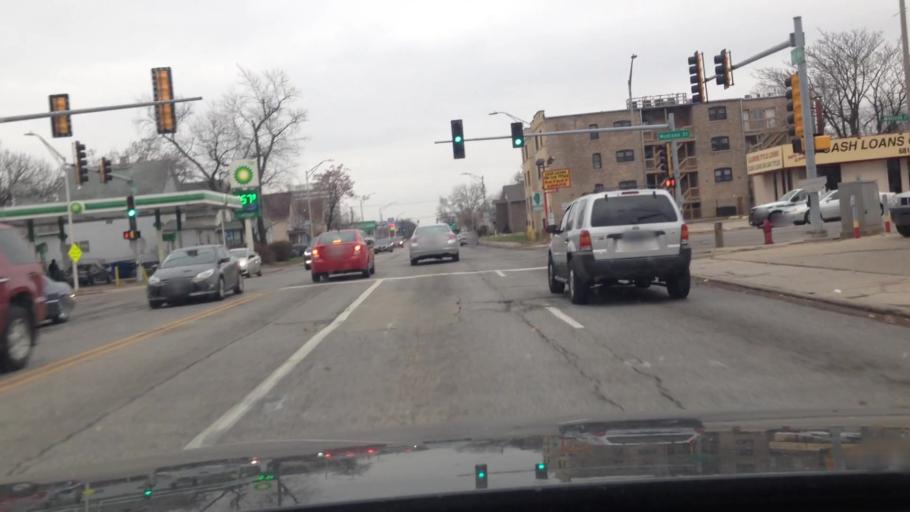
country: US
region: Illinois
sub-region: Cook County
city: Maywood
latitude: 41.8794
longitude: -87.8341
